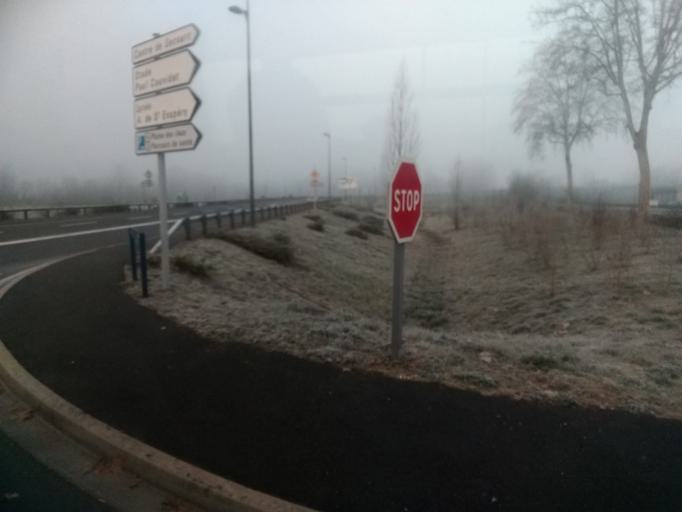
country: FR
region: Aquitaine
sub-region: Departement de la Dordogne
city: Terrasson-Lavilledieu
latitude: 45.1317
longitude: 1.2775
